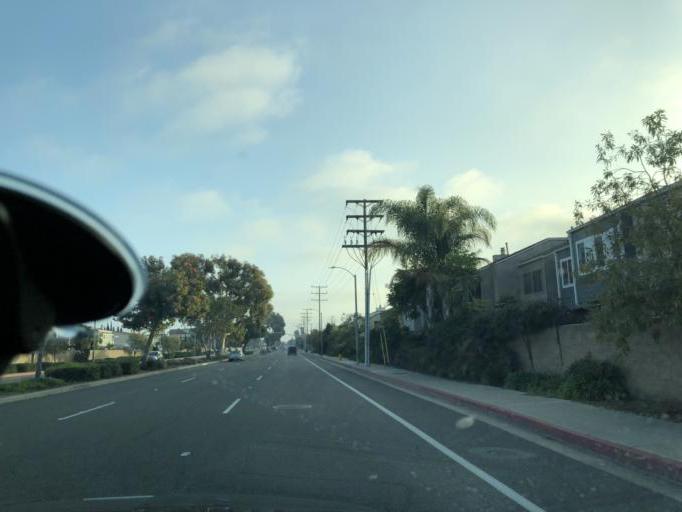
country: US
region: California
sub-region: Orange County
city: Westminster
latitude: 33.7212
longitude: -118.0416
